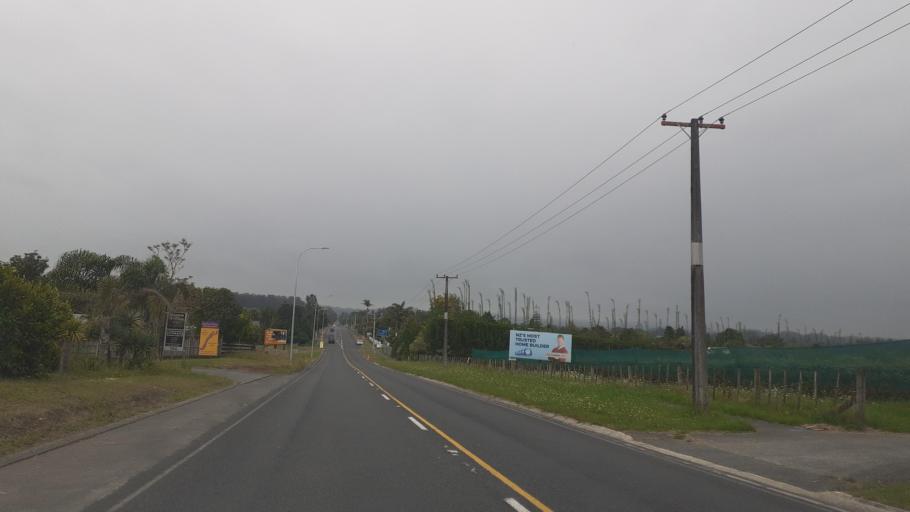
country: NZ
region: Northland
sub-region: Far North District
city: Kerikeri
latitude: -35.2373
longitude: 173.9403
